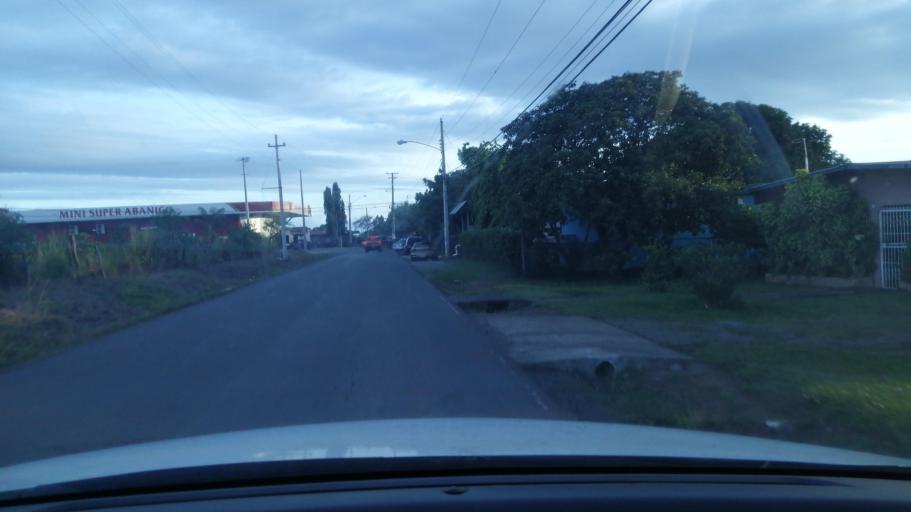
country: PA
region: Chiriqui
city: David
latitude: 8.4027
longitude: -82.4357
